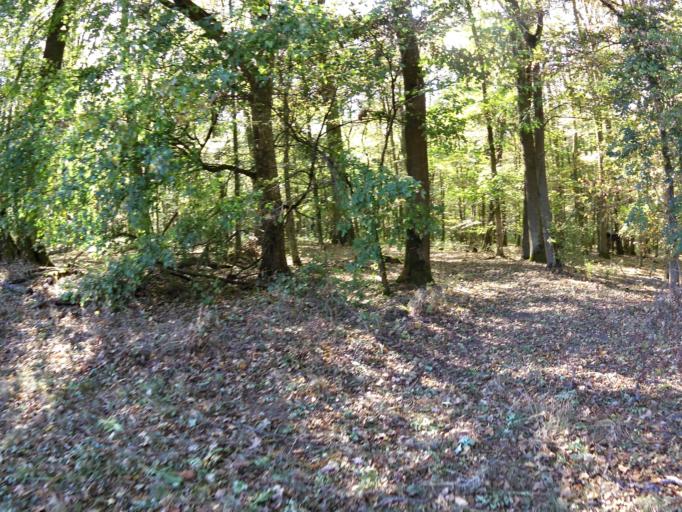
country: DE
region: Bavaria
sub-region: Regierungsbezirk Unterfranken
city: Reichenberg
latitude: 49.7358
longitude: 9.9238
